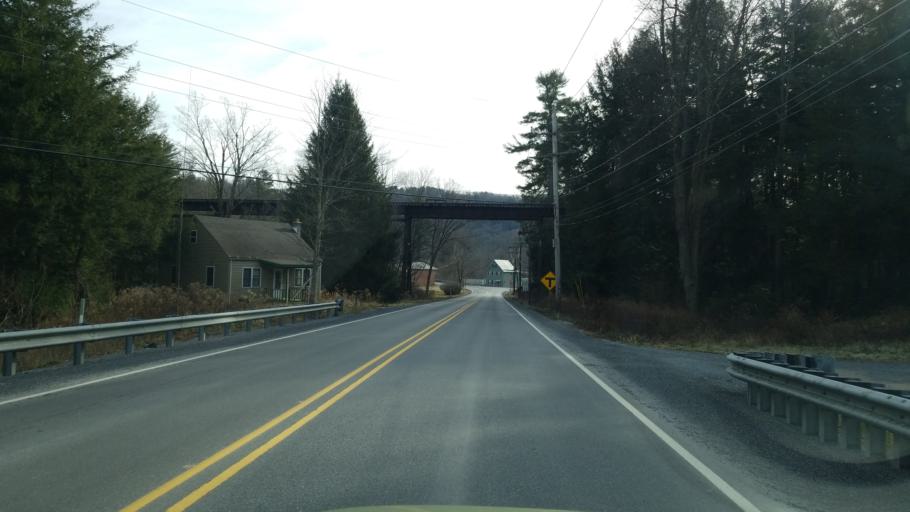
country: US
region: Pennsylvania
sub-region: Indiana County
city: Johnsonburg
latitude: 40.8833
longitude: -78.7648
